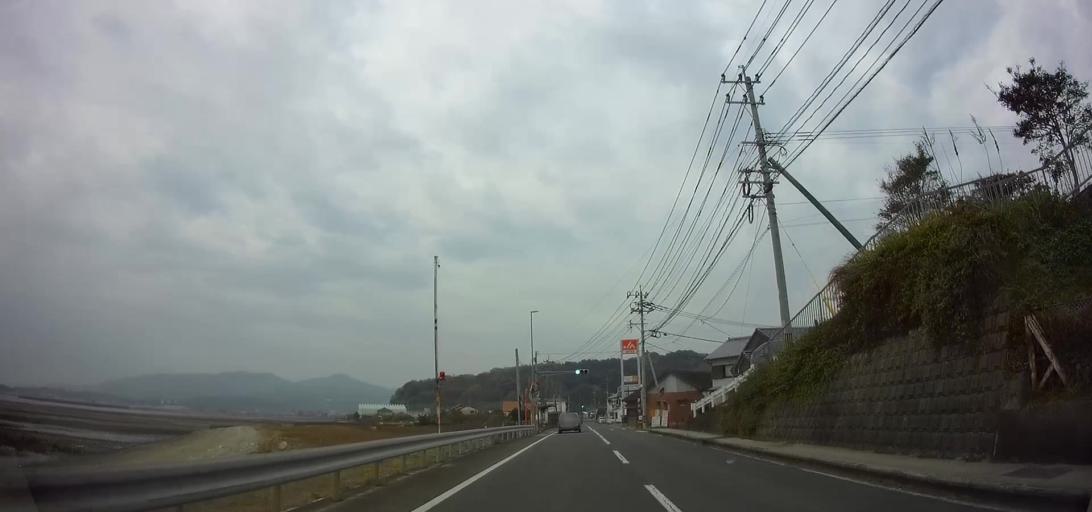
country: JP
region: Nagasaki
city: Shimabara
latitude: 32.6543
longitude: 130.2736
